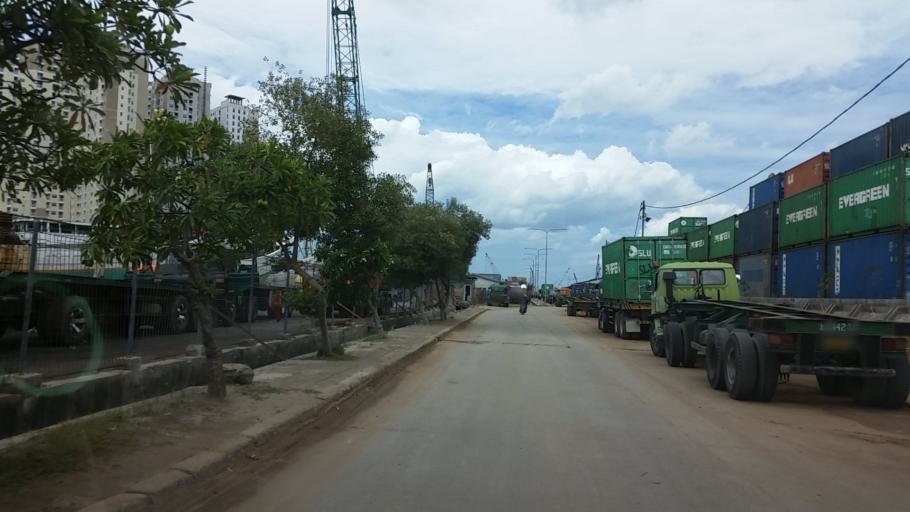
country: ID
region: Jakarta Raya
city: Jakarta
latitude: -6.1220
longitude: 106.8093
